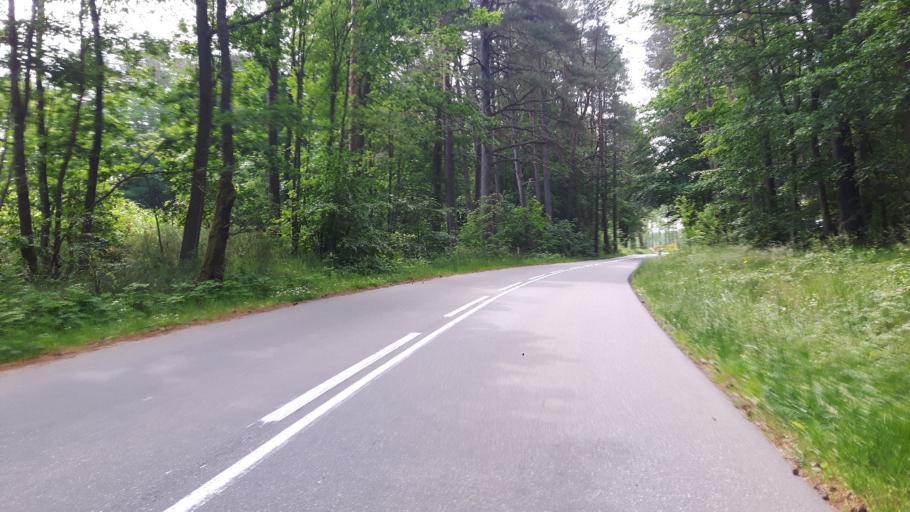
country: PL
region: Pomeranian Voivodeship
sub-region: Powiat leborski
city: Leba
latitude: 54.7503
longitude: 17.7113
